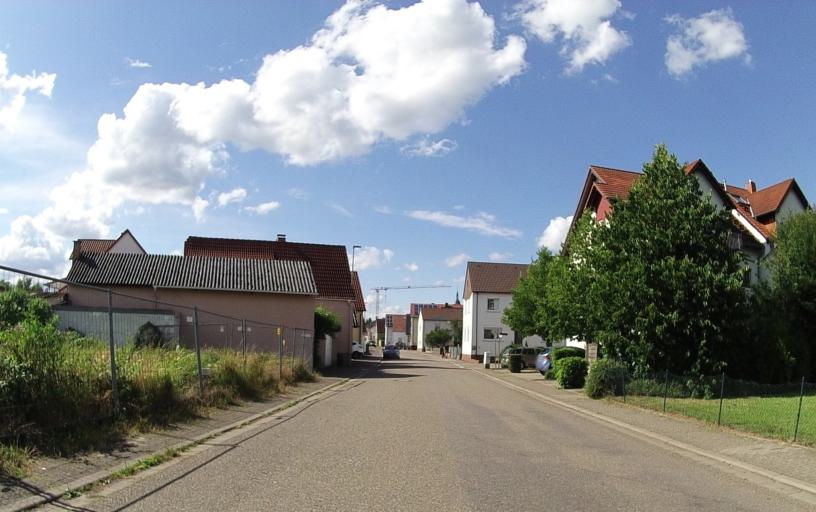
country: DE
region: Rheinland-Pfalz
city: Steinfeld
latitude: 49.0447
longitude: 8.0387
